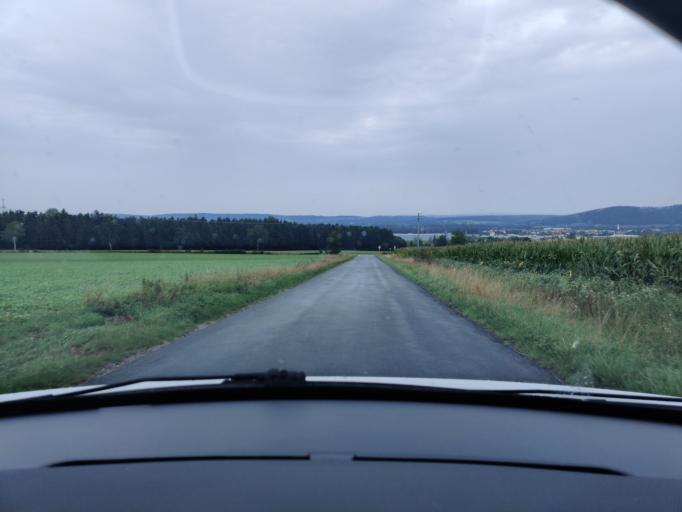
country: DE
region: Bavaria
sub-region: Upper Palatinate
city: Wernberg-Koblitz
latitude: 49.5182
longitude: 12.1419
